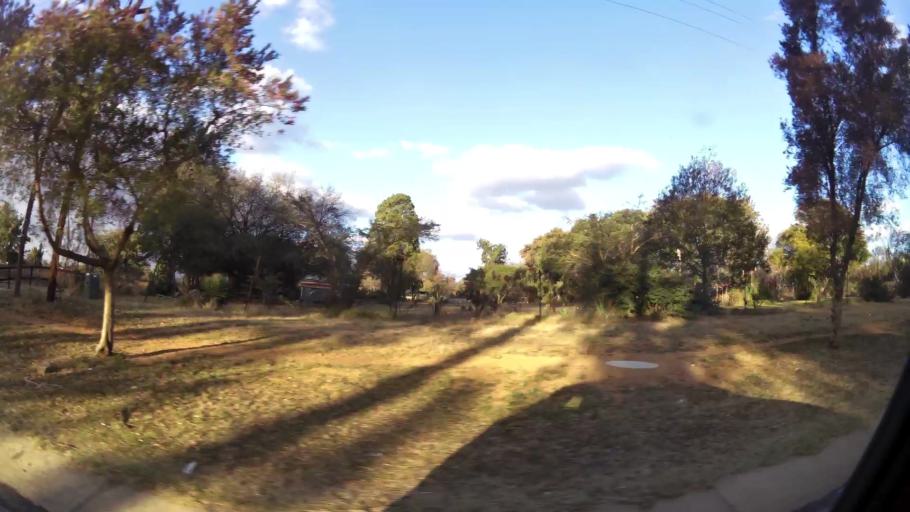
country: ZA
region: Gauteng
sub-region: City of Johannesburg Metropolitan Municipality
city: Midrand
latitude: -25.9534
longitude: 28.1541
